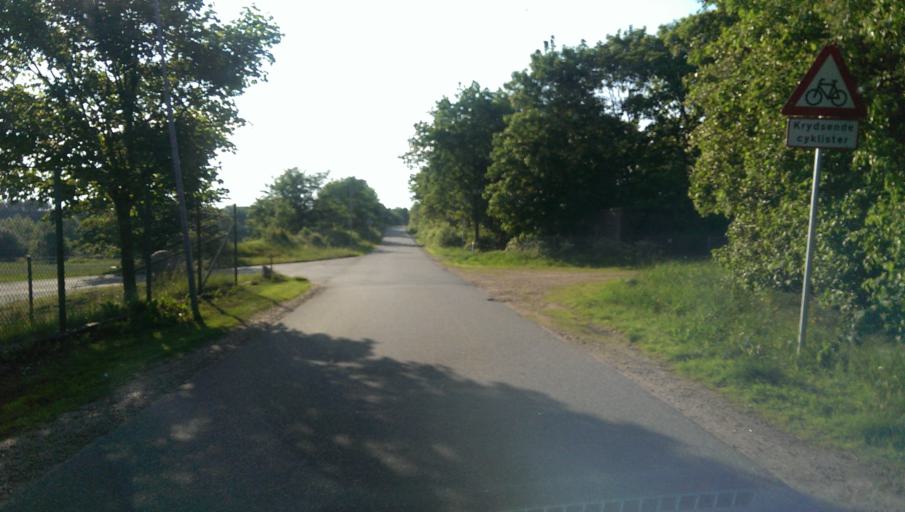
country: DK
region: South Denmark
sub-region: Esbjerg Kommune
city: Tjaereborg
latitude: 55.4672
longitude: 8.5794
